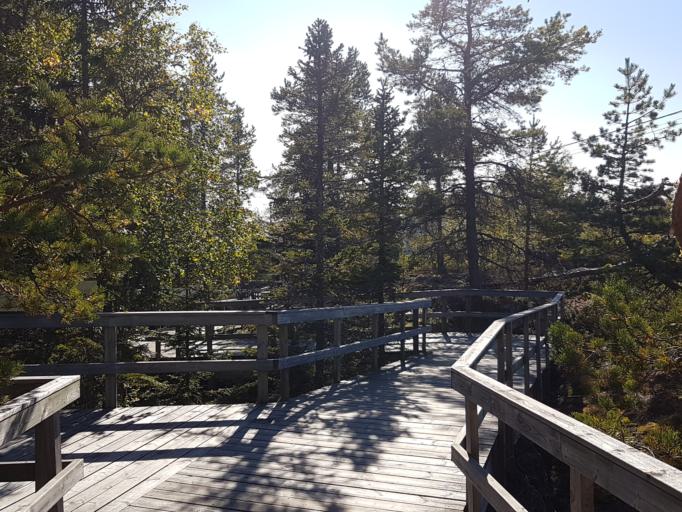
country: SE
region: Vaesterbotten
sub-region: Skelleftea Kommun
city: Skelleftehamn
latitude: 64.4805
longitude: 21.5755
